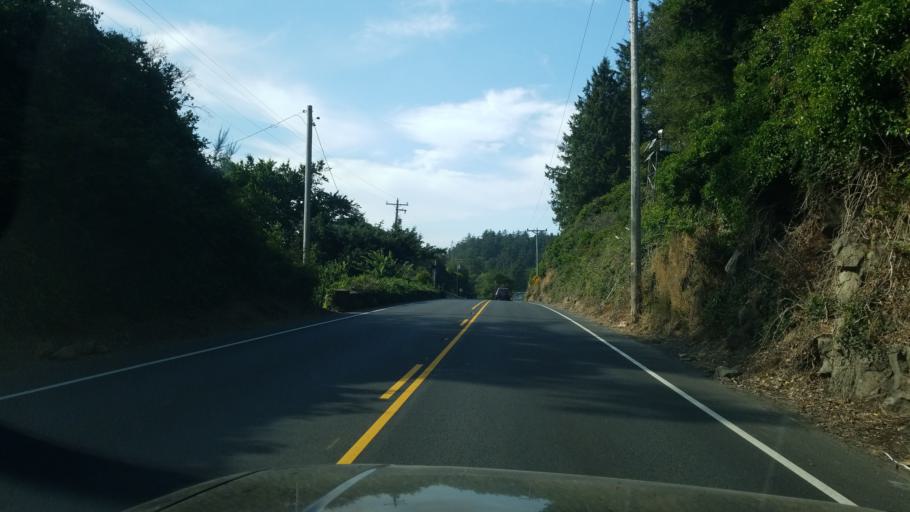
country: US
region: Oregon
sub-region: Tillamook County
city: Rockaway Beach
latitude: 45.5677
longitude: -123.9408
